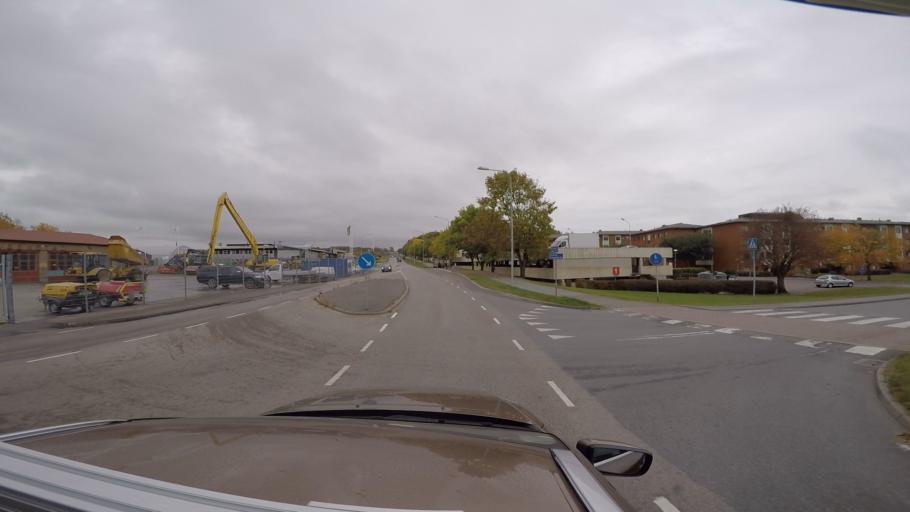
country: SE
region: Vaestra Goetaland
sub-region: Goteborg
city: Majorna
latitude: 57.6443
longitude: 11.9392
